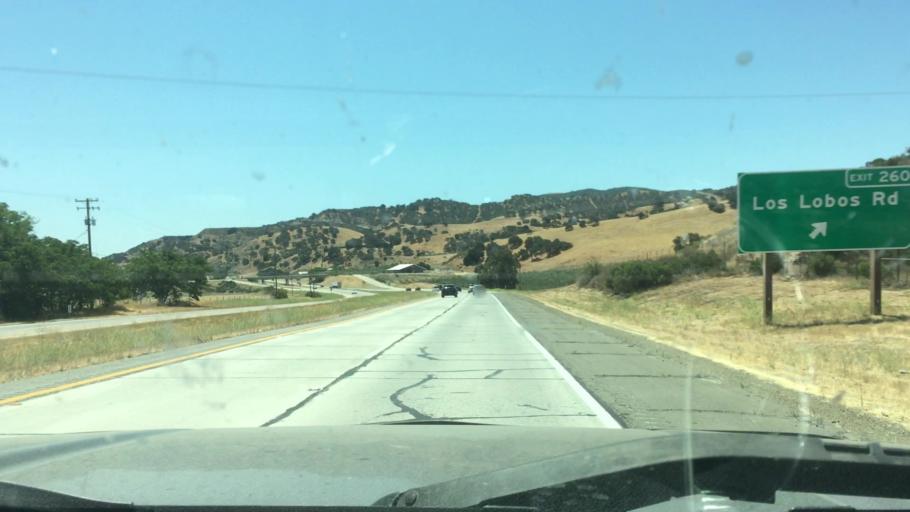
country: US
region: California
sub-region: San Luis Obispo County
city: Lake Nacimiento
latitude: 35.9810
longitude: -120.9026
